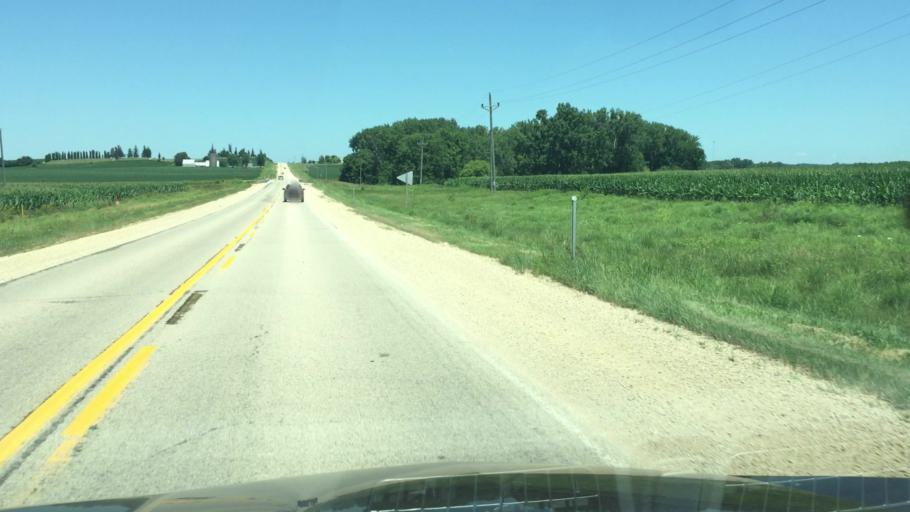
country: US
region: Iowa
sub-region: Cedar County
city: Mechanicsville
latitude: 41.9704
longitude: -91.1419
